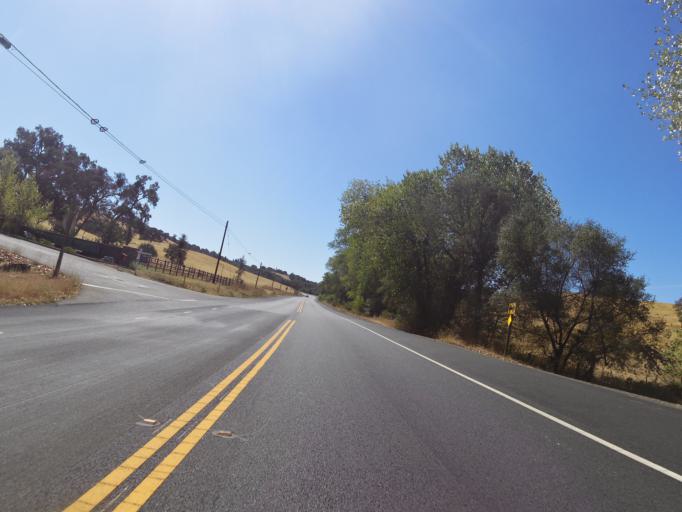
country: US
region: California
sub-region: El Dorado County
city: Deer Park
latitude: 38.6574
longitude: -120.8538
